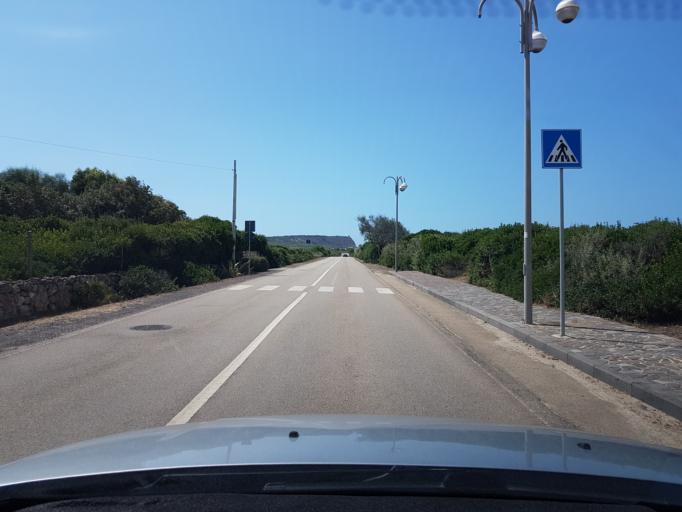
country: IT
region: Sardinia
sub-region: Provincia di Oristano
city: Riola Sardo
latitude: 40.0397
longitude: 8.4118
